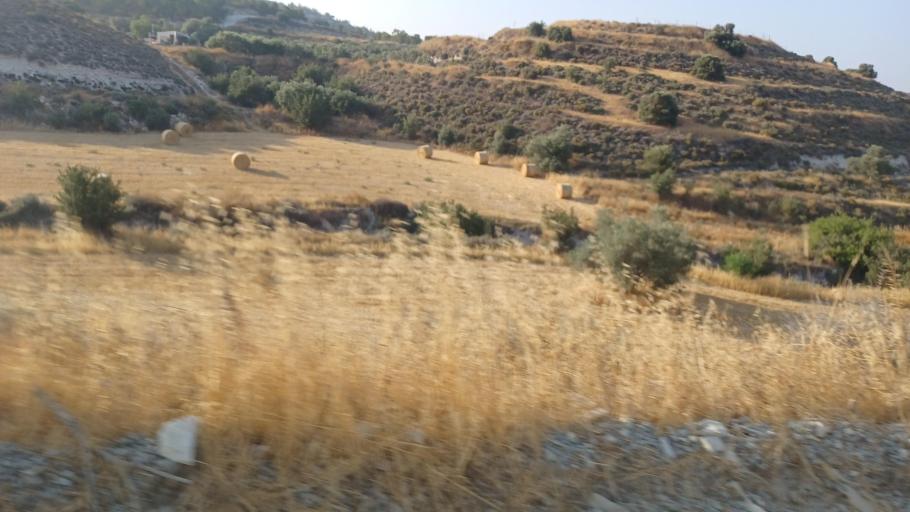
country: CY
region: Larnaka
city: Psevdas
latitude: 34.9386
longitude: 33.5044
